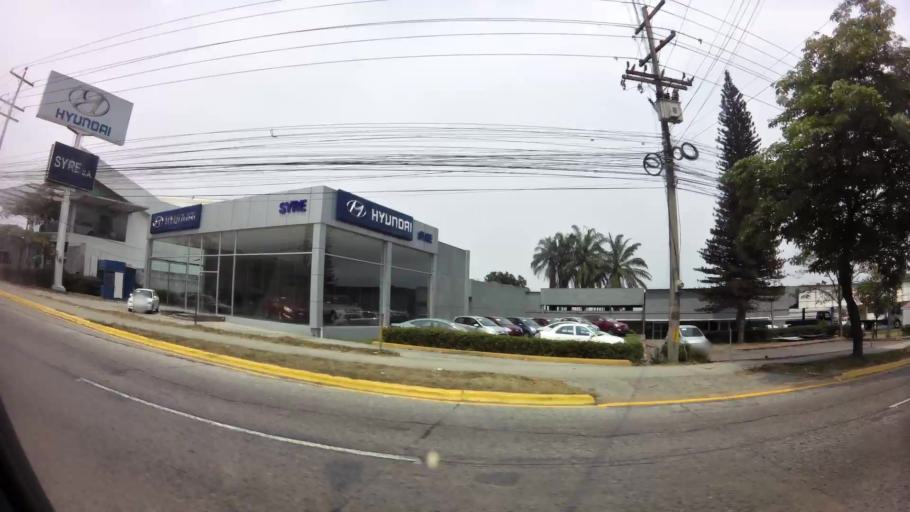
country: HN
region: Cortes
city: Armenta
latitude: 15.4766
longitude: -88.0339
